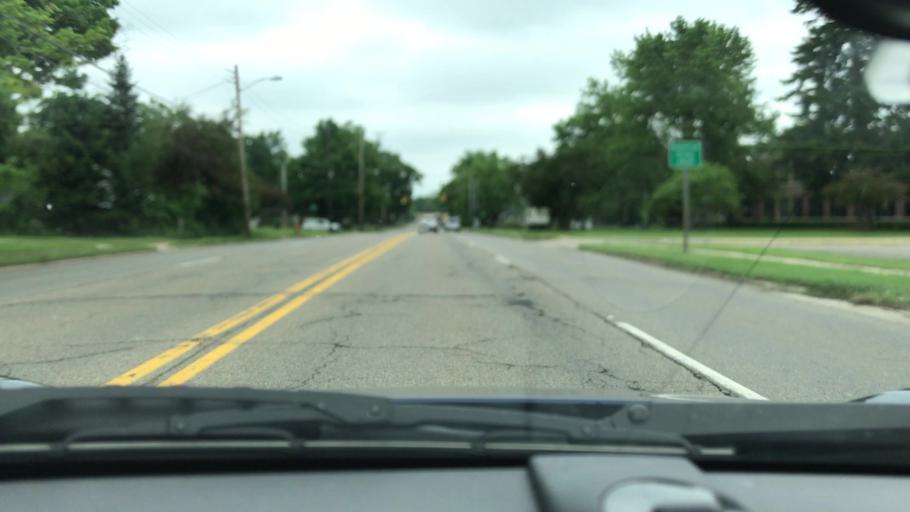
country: US
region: Michigan
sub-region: Calhoun County
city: Springfield
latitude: 42.3492
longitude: -85.2299
